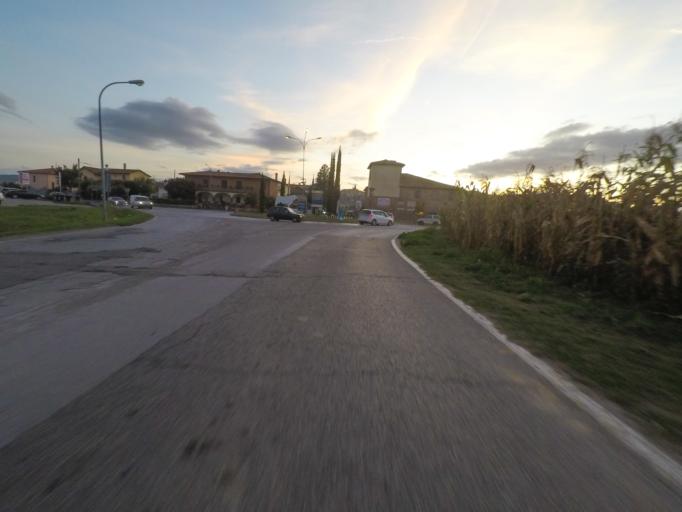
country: IT
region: Tuscany
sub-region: Provincia di Siena
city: Sinalunga
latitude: 43.2212
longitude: 11.7550
